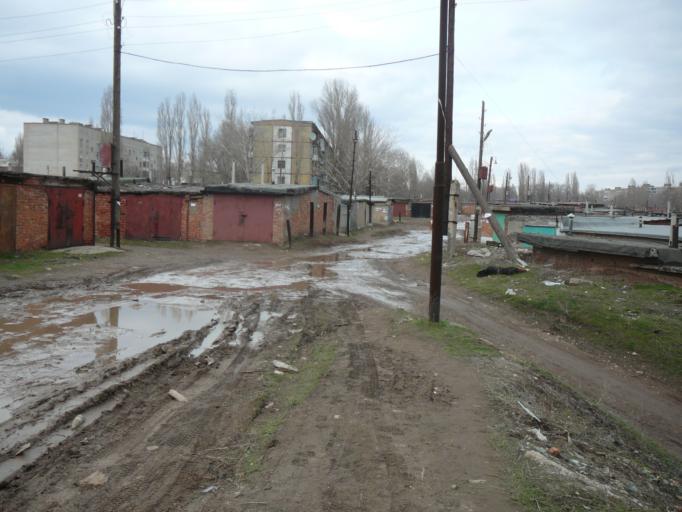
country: RU
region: Saratov
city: Engel's
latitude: 51.4676
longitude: 46.1051
